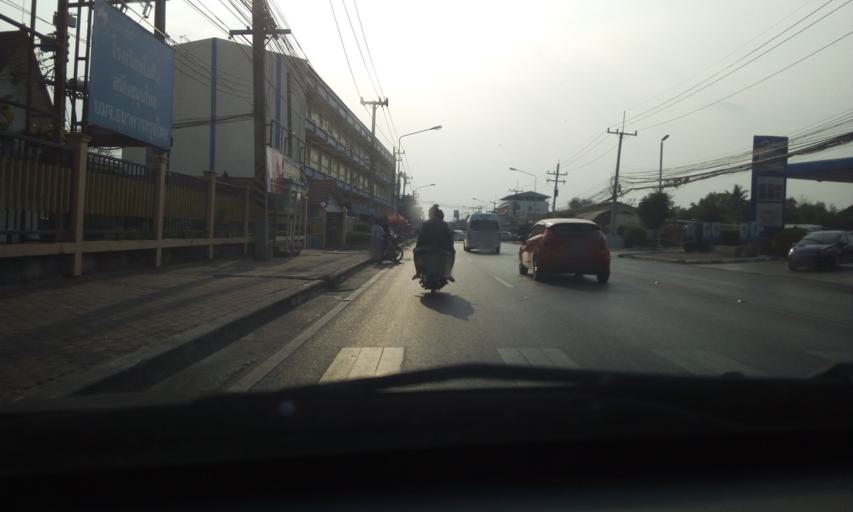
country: TH
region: Nakhon Nayok
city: Nakhon Nayok
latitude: 14.2029
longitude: 101.2047
